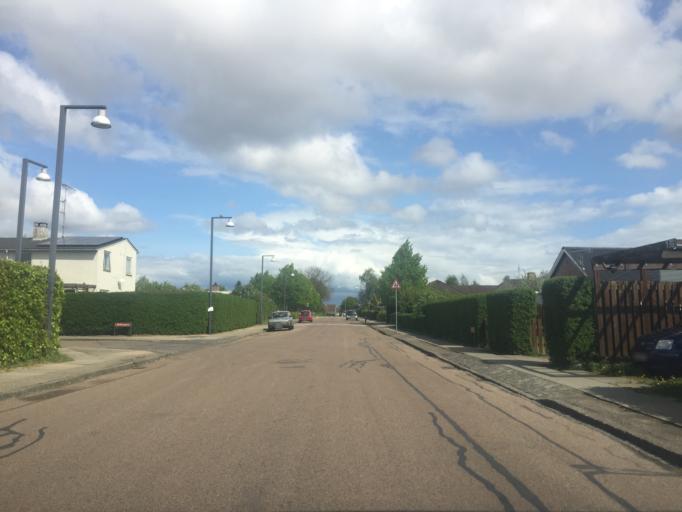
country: DK
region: Capital Region
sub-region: Rodovre Kommune
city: Rodovre
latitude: 55.6871
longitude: 12.4447
